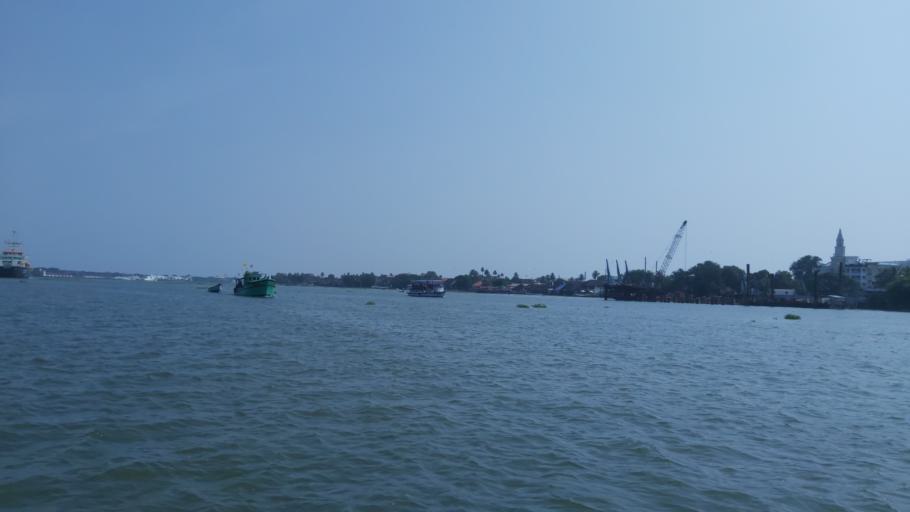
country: IN
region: Kerala
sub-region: Ernakulam
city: Cochin
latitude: 9.9704
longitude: 76.2529
